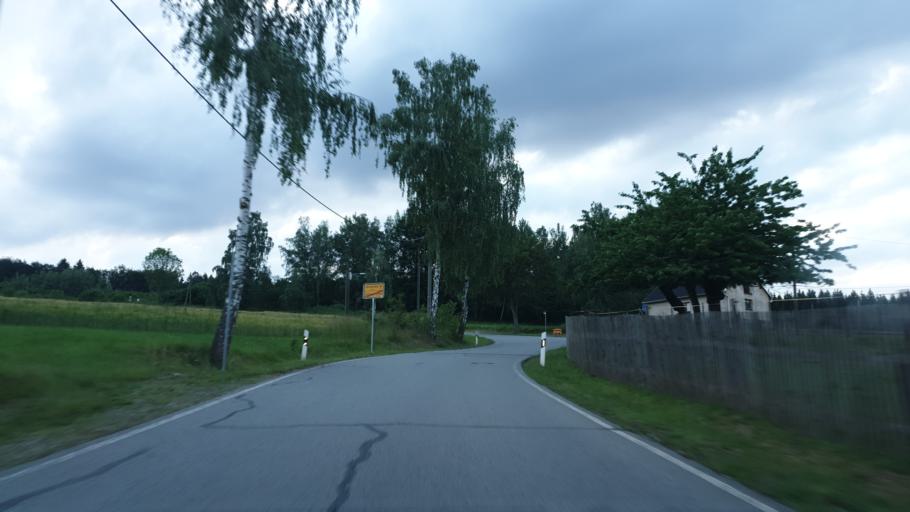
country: DE
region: Saxony
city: Lossnitz
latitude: 50.6300
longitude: 12.7093
